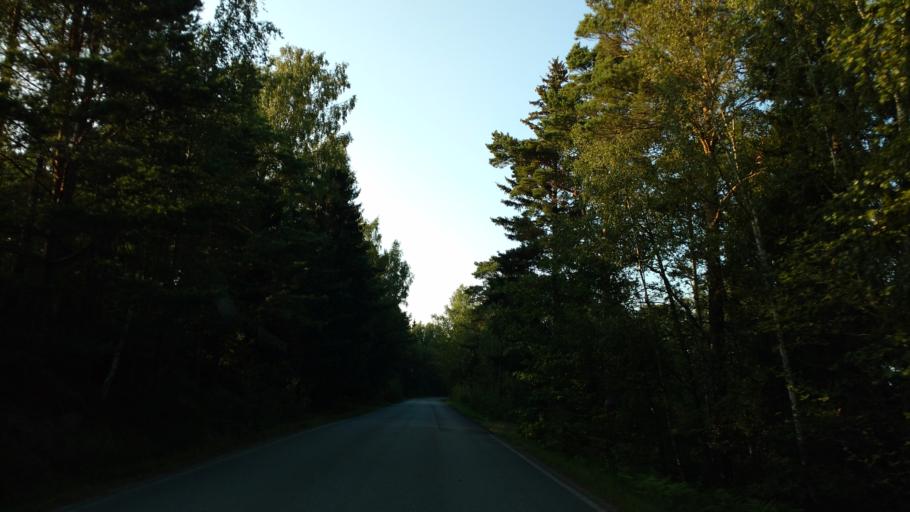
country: FI
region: Varsinais-Suomi
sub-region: Aboland-Turunmaa
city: Dragsfjaerd
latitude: 59.9761
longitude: 22.4493
